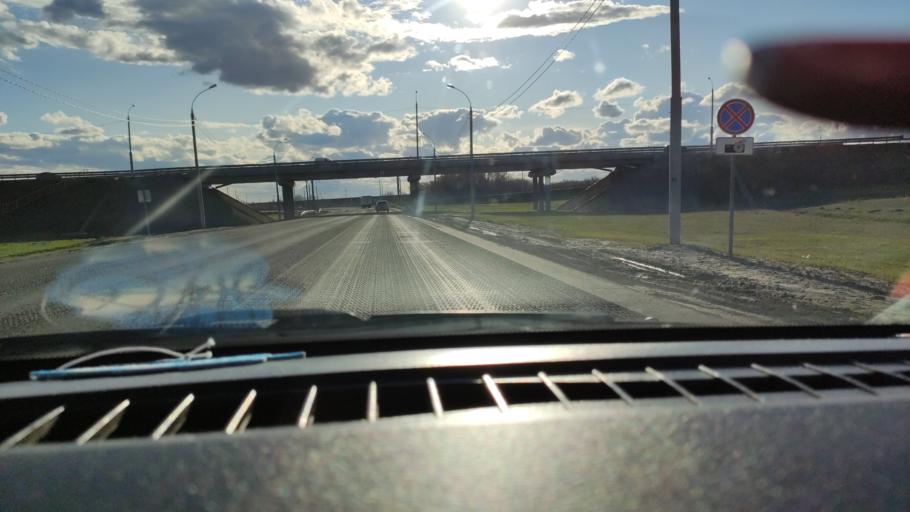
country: RU
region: Saratov
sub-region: Saratovskiy Rayon
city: Saratov
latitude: 51.7733
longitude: 46.0866
